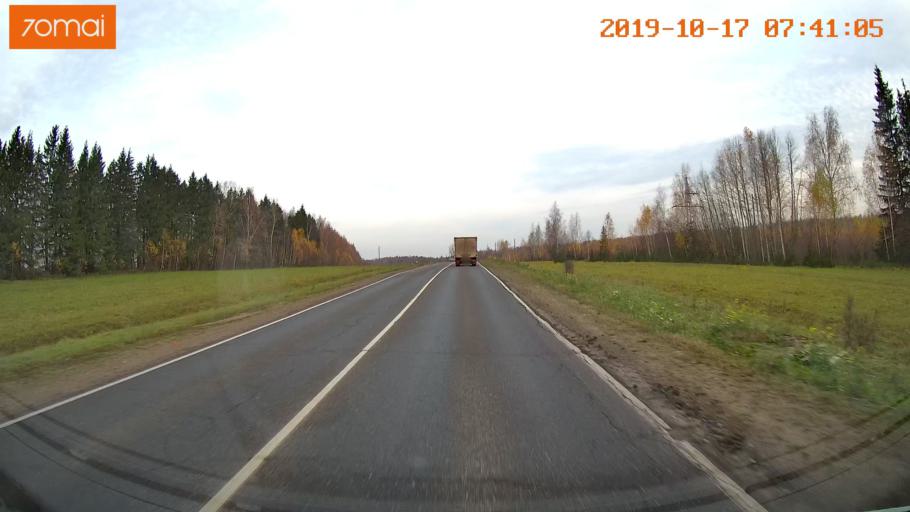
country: RU
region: Vladimir
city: Yur'yev-Pol'skiy
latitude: 56.4793
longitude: 39.8173
